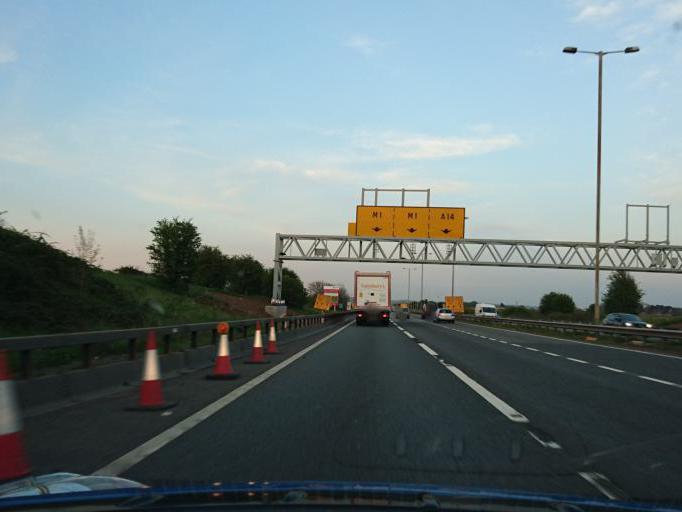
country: GB
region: England
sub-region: Leicestershire
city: Lutterworth
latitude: 52.4057
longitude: -1.1991
